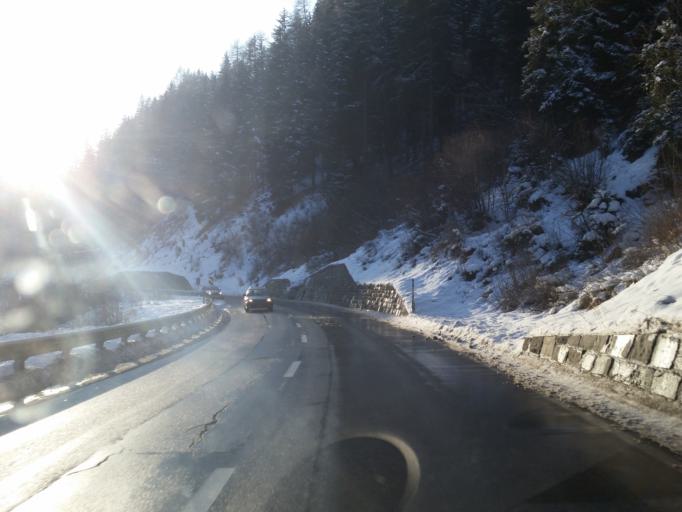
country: CH
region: Grisons
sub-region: Inn District
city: Scuol
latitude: 46.7860
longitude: 10.2587
